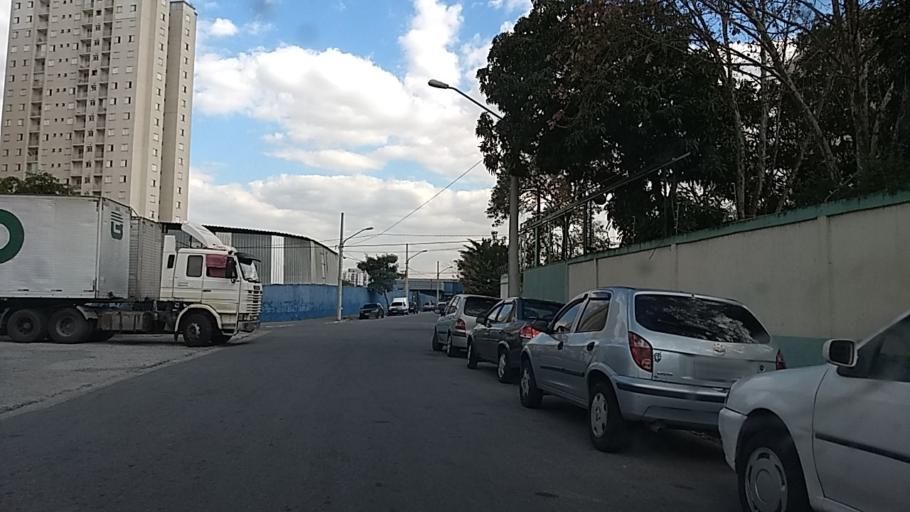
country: BR
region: Sao Paulo
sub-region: Sao Paulo
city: Sao Paulo
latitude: -23.5183
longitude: -46.6017
